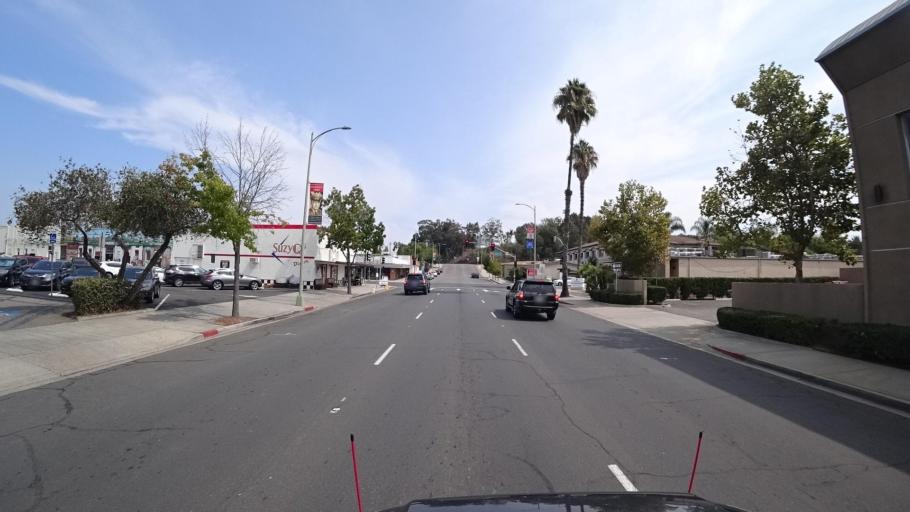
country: US
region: California
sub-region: San Diego County
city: Escondido
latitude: 33.1218
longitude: -117.0787
